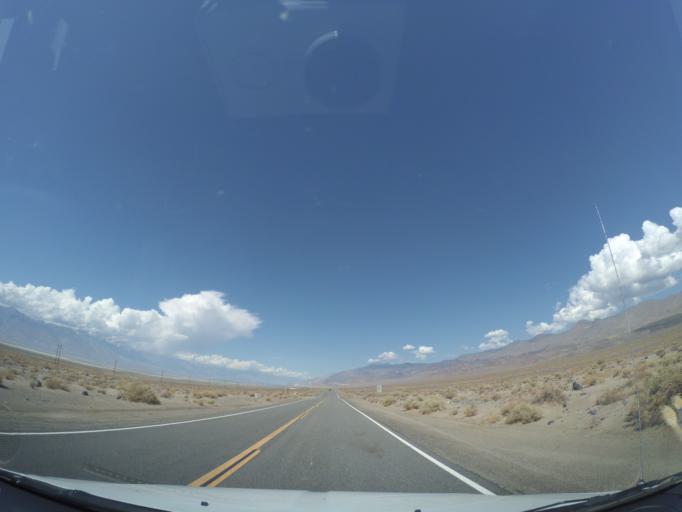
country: US
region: California
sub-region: Inyo County
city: Lone Pine
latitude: 36.4308
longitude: -117.8250
